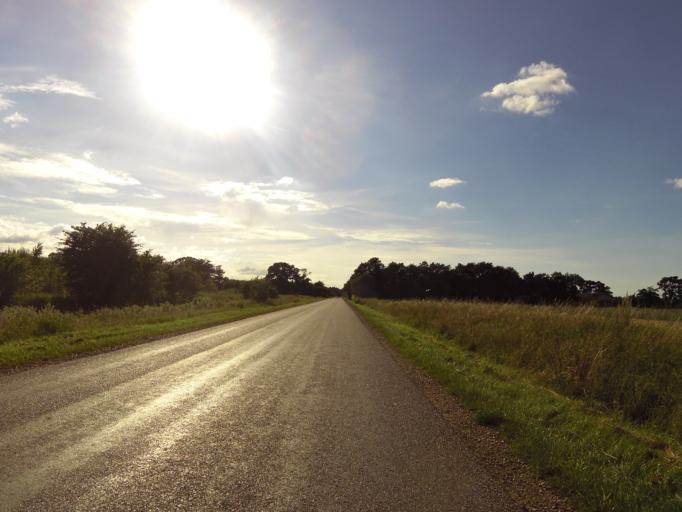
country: DK
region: South Denmark
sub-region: Haderslev Kommune
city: Vojens
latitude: 55.2087
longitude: 9.2550
